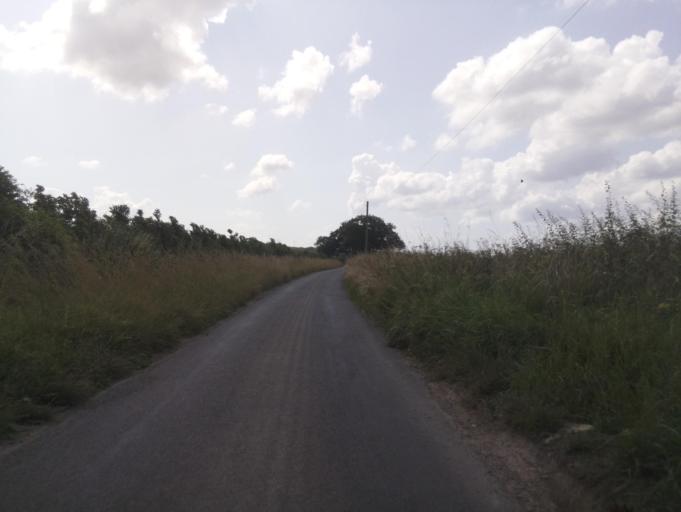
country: GB
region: England
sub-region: Wiltshire
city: Malmesbury
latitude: 51.5656
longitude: -2.1230
